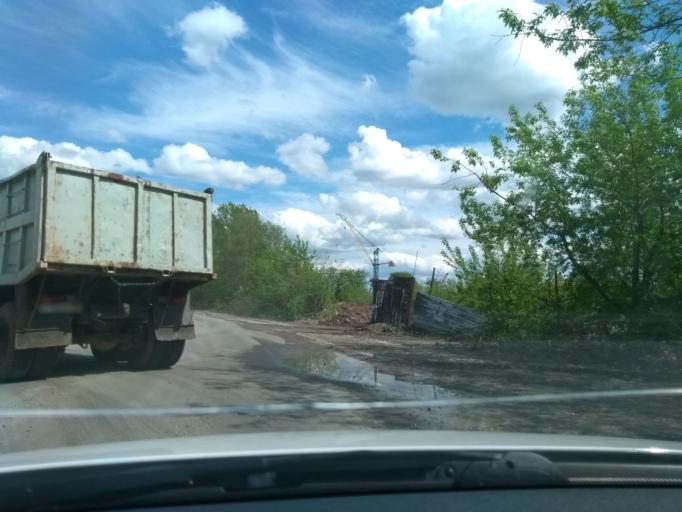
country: RU
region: Perm
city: Kondratovo
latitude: 58.0106
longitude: 56.0663
